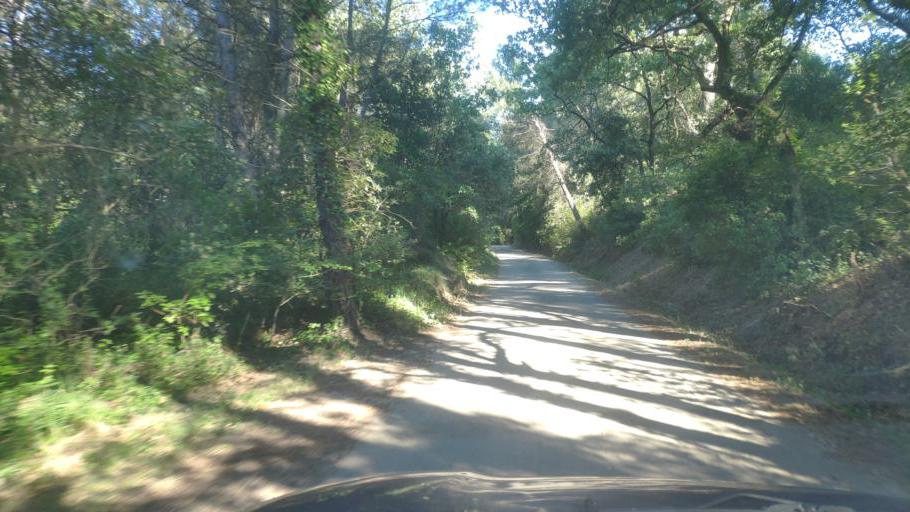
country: FR
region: Provence-Alpes-Cote d'Azur
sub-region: Departement du Vaucluse
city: Aubignan
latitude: 44.0845
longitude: 5.0413
